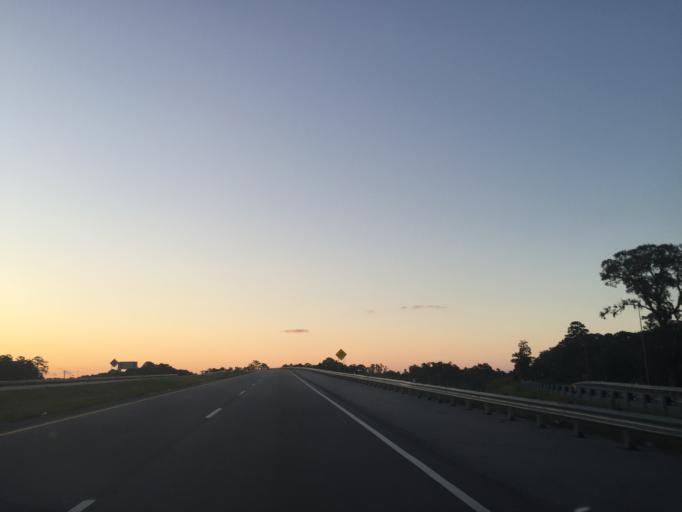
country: US
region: Georgia
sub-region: Chatham County
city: Montgomery
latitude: 31.9740
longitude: -81.1089
